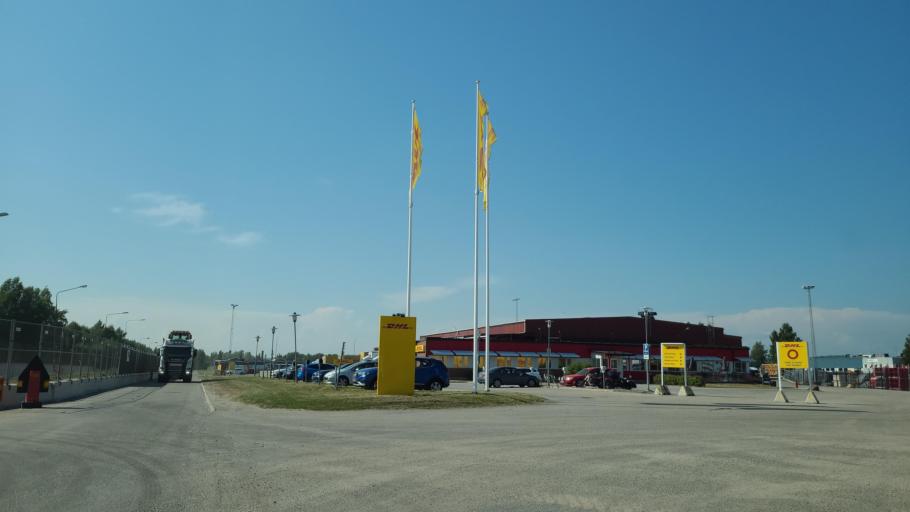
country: SE
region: Vaesterbotten
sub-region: Umea Kommun
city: Umea
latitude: 63.8432
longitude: 20.2199
